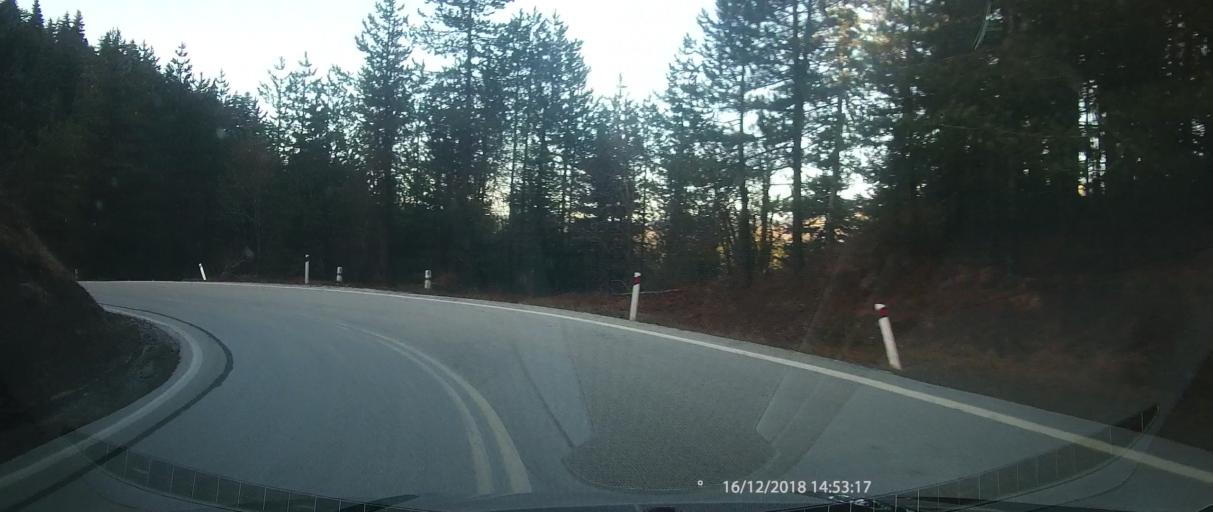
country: GR
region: West Macedonia
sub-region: Nomos Kastorias
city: Nestorio
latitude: 40.2091
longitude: 21.0584
